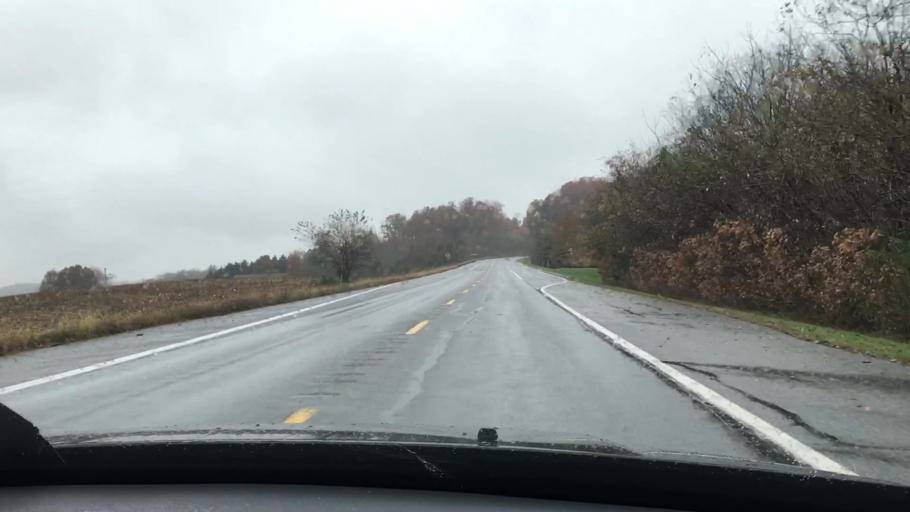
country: US
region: Maryland
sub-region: Frederick County
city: Buckeystown
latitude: 39.3241
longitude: -77.4183
